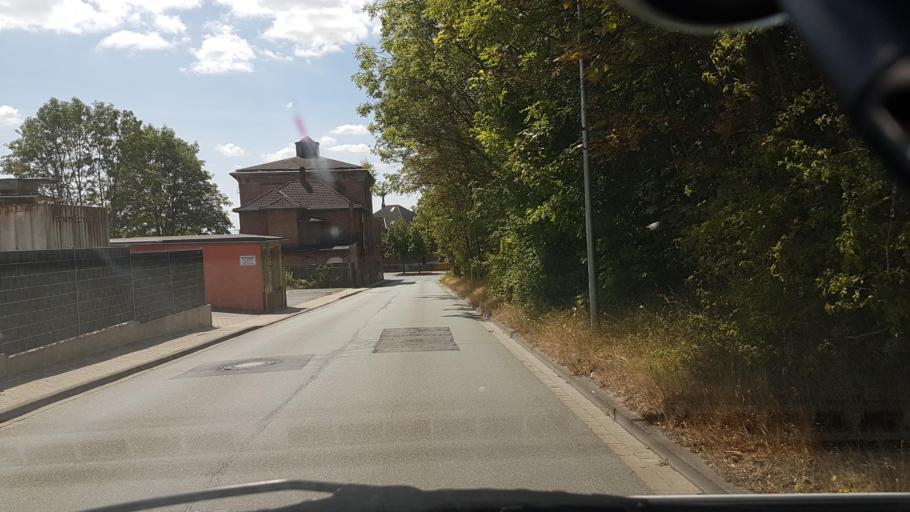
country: DE
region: Lower Saxony
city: Schoningen
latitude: 52.1334
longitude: 10.9747
